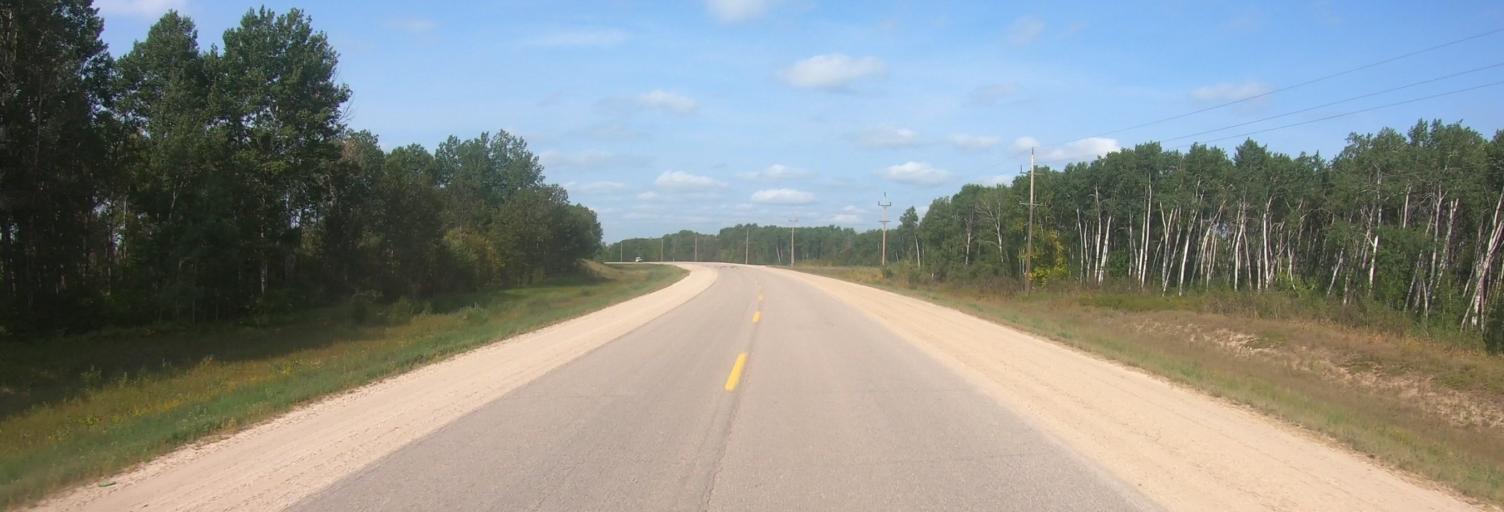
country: CA
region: Manitoba
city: La Broquerie
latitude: 49.1811
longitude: -96.2036
